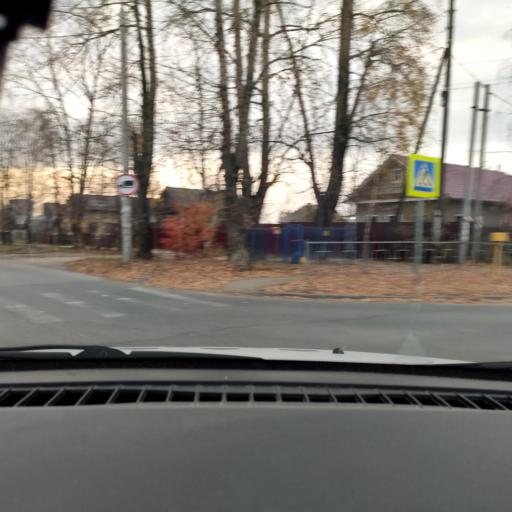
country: RU
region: Perm
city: Polazna
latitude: 58.1230
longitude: 56.4041
